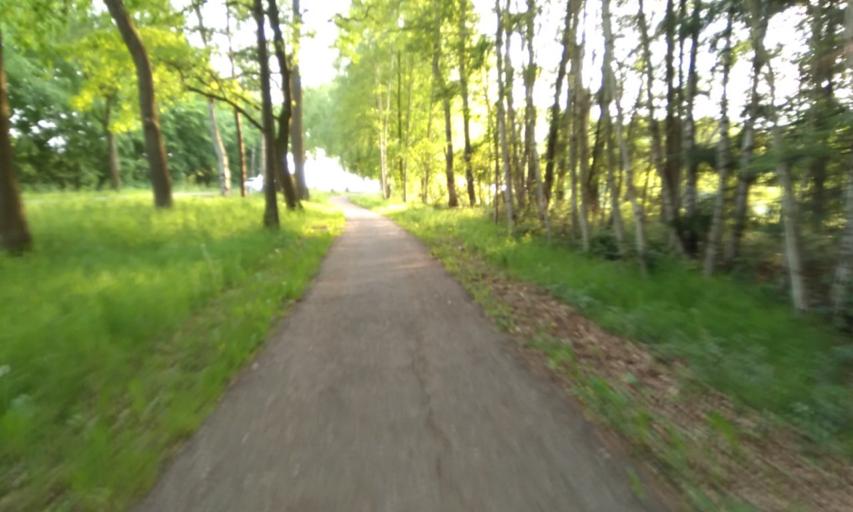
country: DE
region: Lower Saxony
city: Bliedersdorf
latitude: 53.4638
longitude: 9.5475
